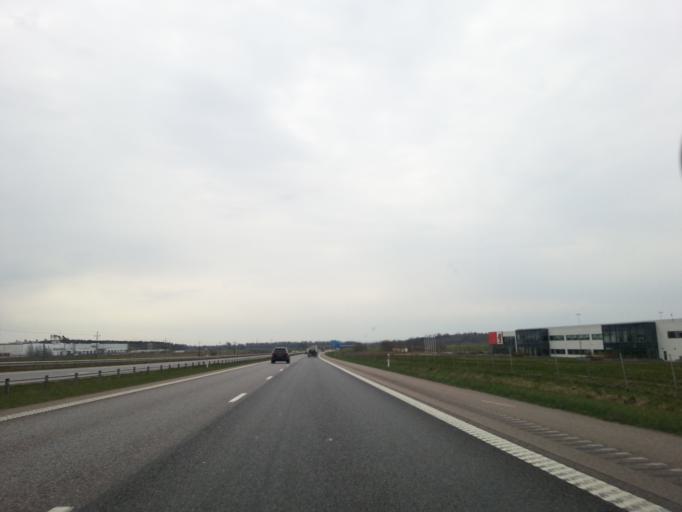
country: SE
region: Halland
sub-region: Halmstads Kommun
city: Halmstad
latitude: 56.7238
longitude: 12.8830
